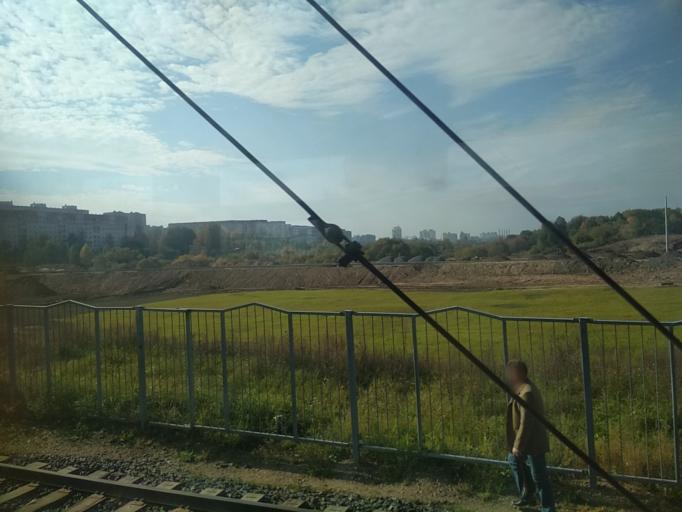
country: BY
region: Minsk
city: Syenitsa
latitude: 53.8572
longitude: 27.5582
